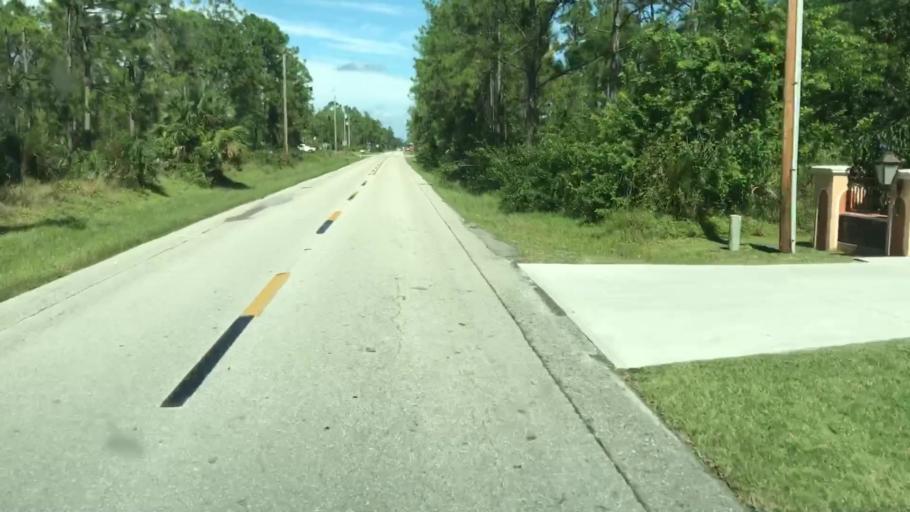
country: US
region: Florida
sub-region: Lee County
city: Lehigh Acres
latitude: 26.6410
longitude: -81.6465
